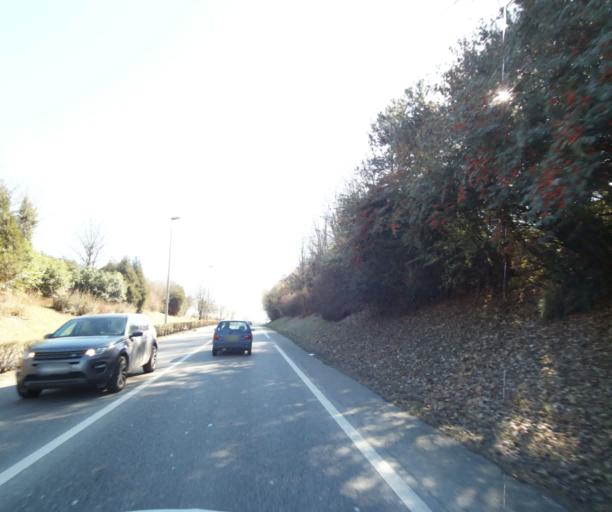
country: FR
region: Lorraine
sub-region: Departement de Meurthe-et-Moselle
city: Vandoeuvre-les-Nancy
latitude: 48.6570
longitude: 6.1782
